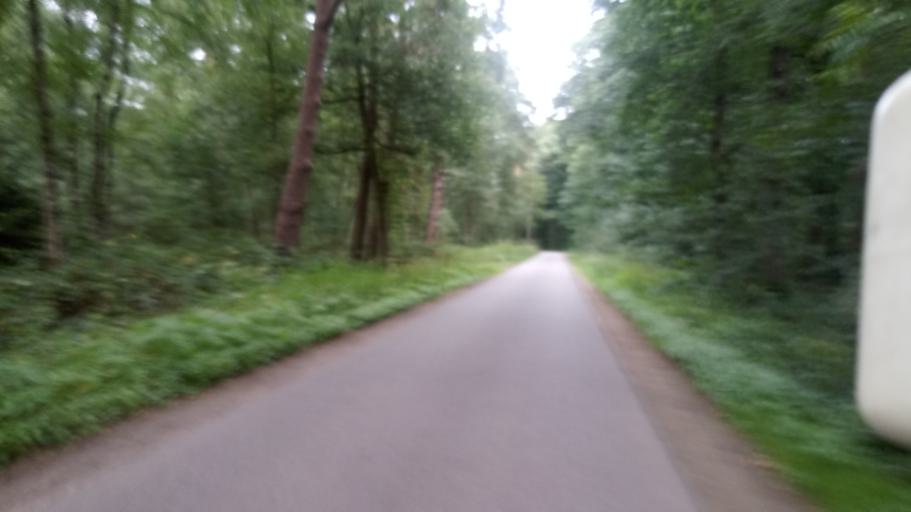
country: NL
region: Gelderland
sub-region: Gemeente Voorst
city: Voorst
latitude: 52.1770
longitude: 6.1110
